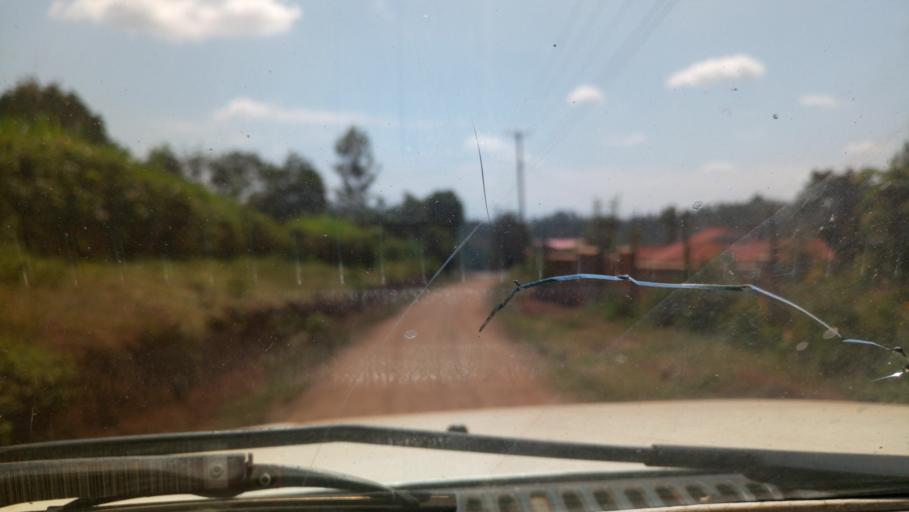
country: KE
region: Murang'a District
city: Murang'a
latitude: -0.6611
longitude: 37.1030
